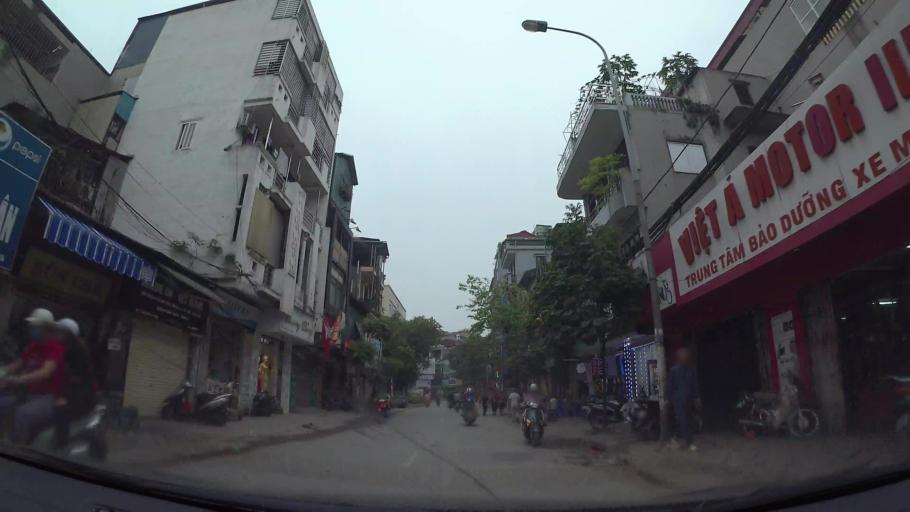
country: VN
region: Ha Noi
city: Hai BaTrung
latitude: 20.9897
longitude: 105.8456
